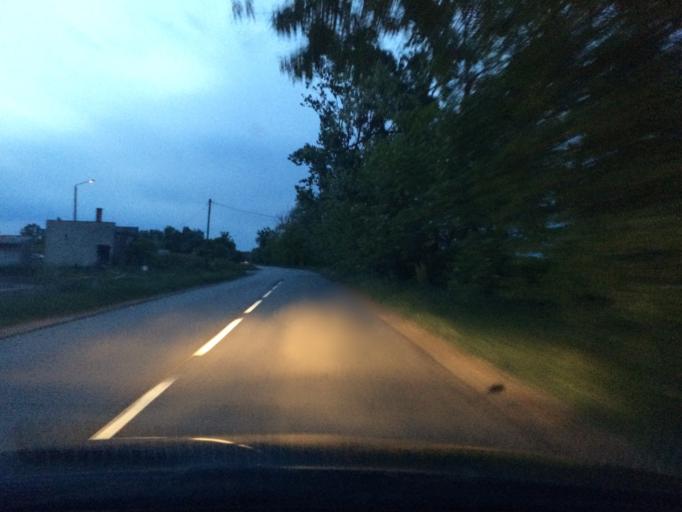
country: HU
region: Szabolcs-Szatmar-Bereg
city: Tiszavasvari
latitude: 47.9348
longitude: 21.3835
